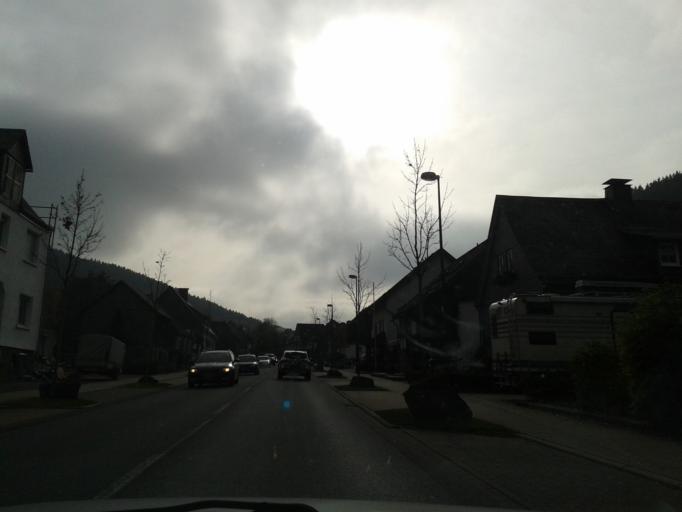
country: DE
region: North Rhine-Westphalia
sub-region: Regierungsbezirk Arnsberg
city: Winterberg
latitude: 51.2578
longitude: 8.5282
